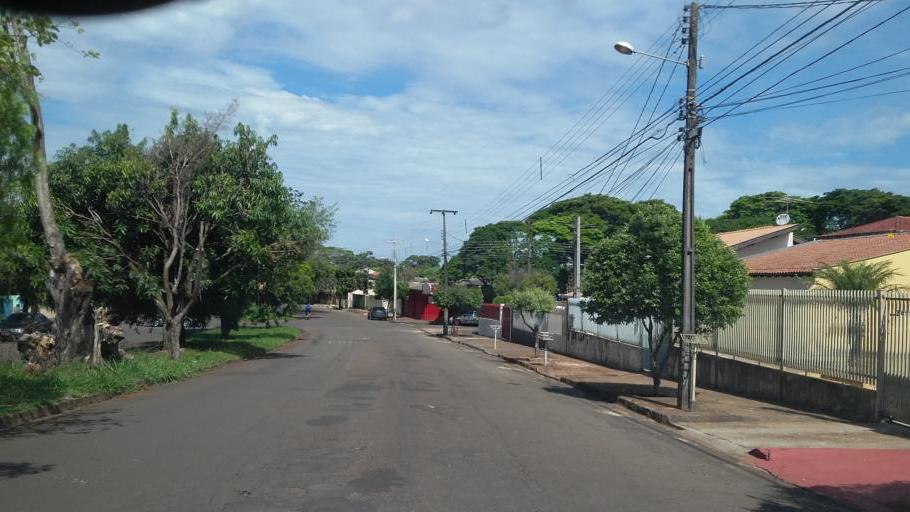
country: BR
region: Parana
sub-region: Londrina
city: Londrina
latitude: -23.2849
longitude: -51.2037
